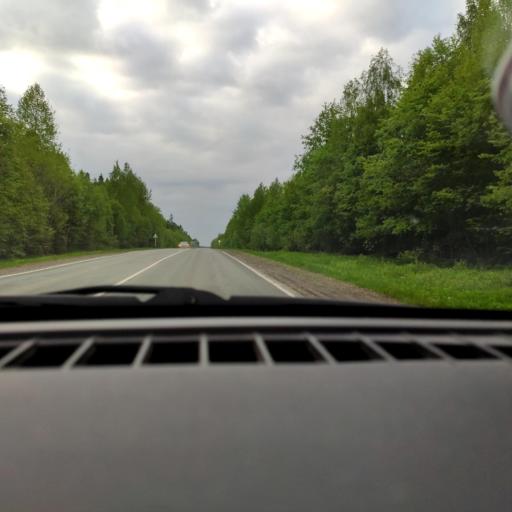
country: RU
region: Perm
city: Perm
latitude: 58.1789
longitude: 56.2267
